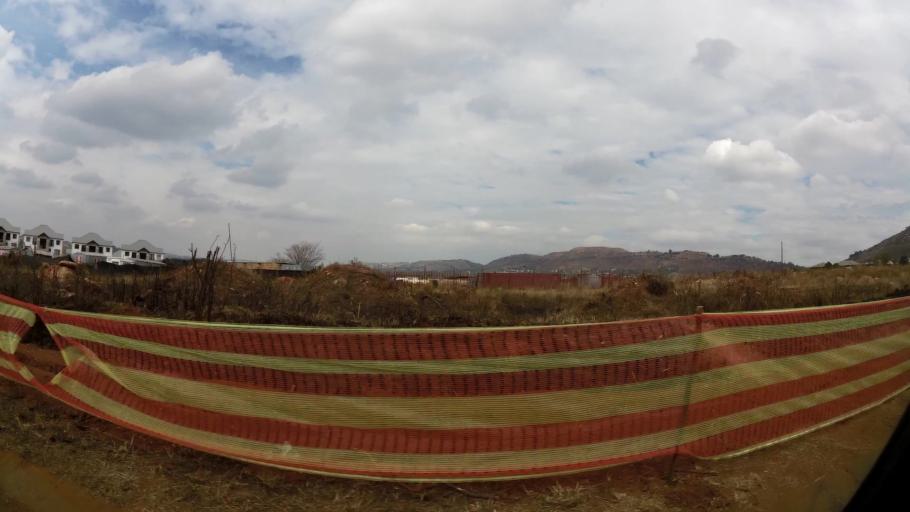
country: ZA
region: Gauteng
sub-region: City of Johannesburg Metropolitan Municipality
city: Roodepoort
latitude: -26.1023
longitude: 27.8820
